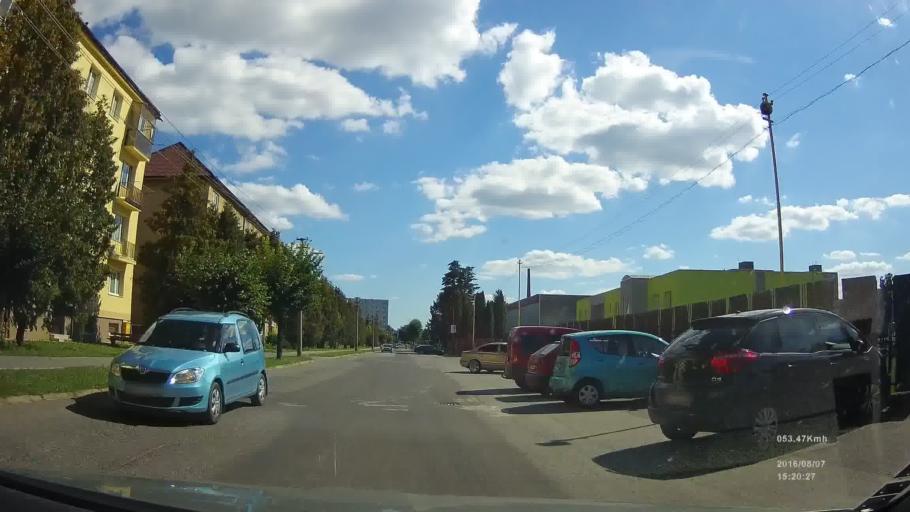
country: SK
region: Presovsky
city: Stropkov
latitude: 49.2021
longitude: 21.6483
